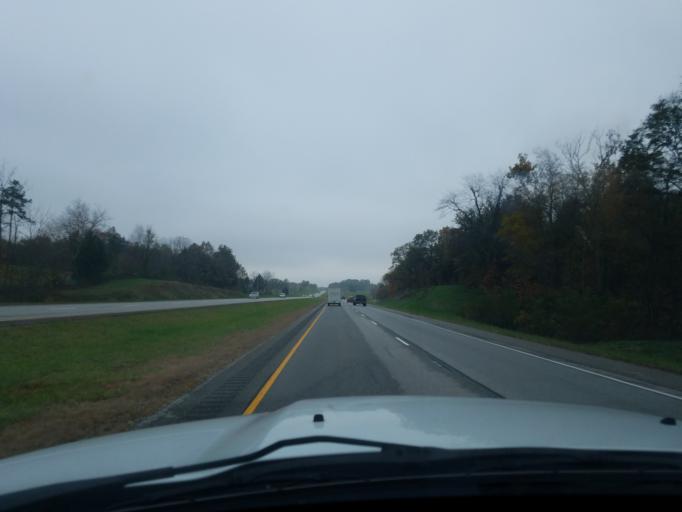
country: US
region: Kentucky
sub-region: Hardin County
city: Elizabethtown
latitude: 37.6214
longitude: -85.8124
